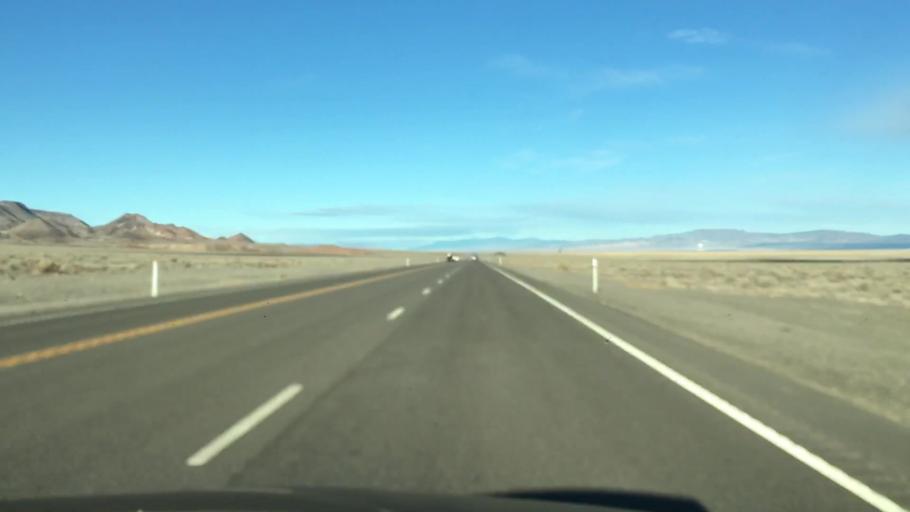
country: US
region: Nevada
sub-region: Nye County
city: Tonopah
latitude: 38.0521
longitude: -117.6557
